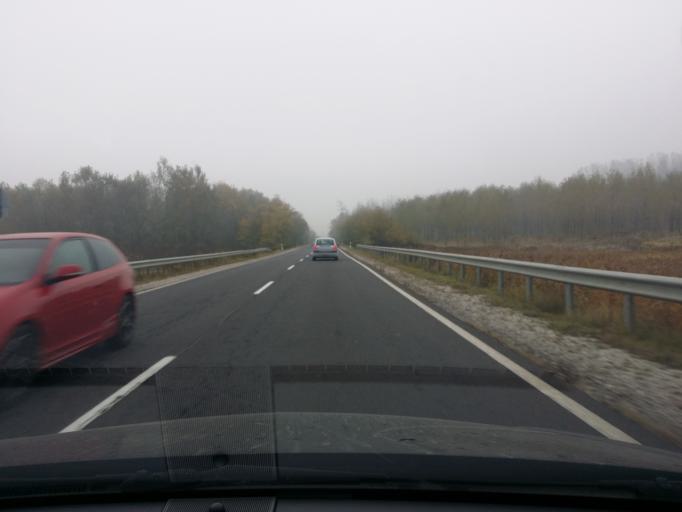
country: HU
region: Szabolcs-Szatmar-Bereg
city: Nyirbogdany
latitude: 48.0339
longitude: 21.8557
